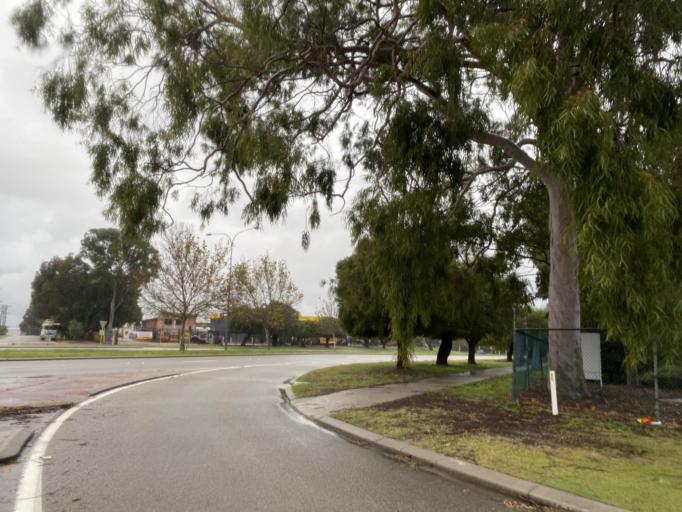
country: AU
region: Western Australia
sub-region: Canning
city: Queens Park
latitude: -31.9964
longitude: 115.9579
